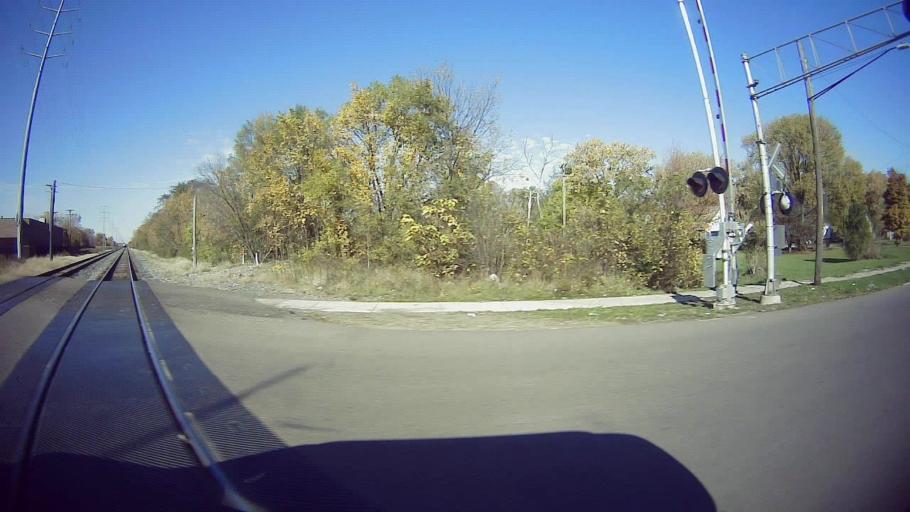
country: US
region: Michigan
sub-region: Wayne County
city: Dearborn
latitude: 42.3580
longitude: -83.2075
